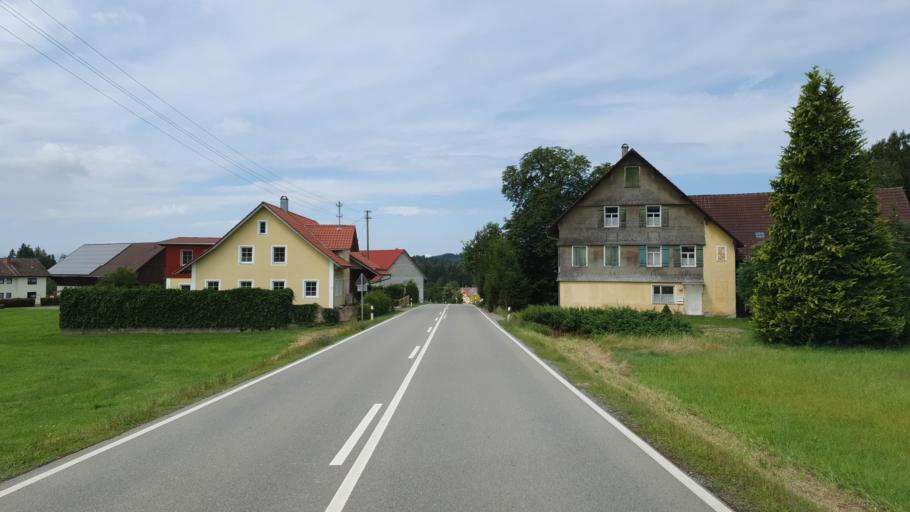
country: AT
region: Vorarlberg
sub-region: Politischer Bezirk Bregenz
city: Hohenweiler
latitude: 47.5972
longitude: 9.7903
